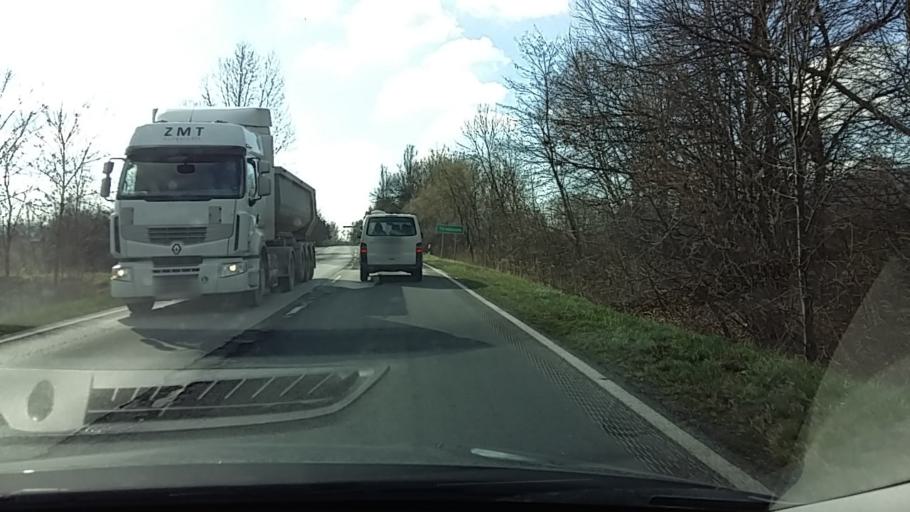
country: HU
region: Veszprem
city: Tapolca
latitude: 46.8383
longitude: 17.3720
